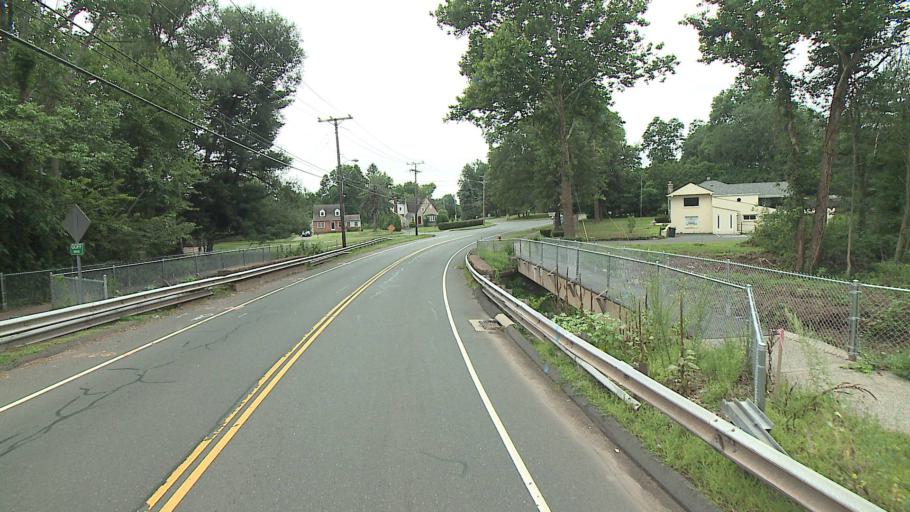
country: US
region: Connecticut
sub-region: Hartford County
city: Wethersfield
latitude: 41.6896
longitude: -72.6586
